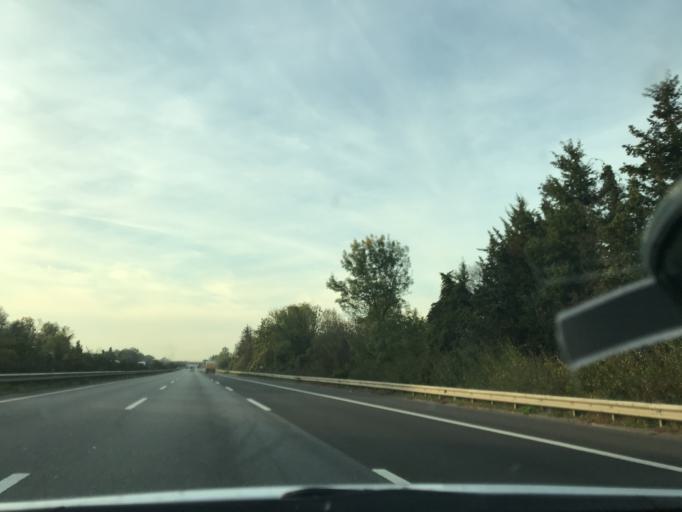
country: TR
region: Duzce
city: Cilimli
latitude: 40.8234
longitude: 31.0630
